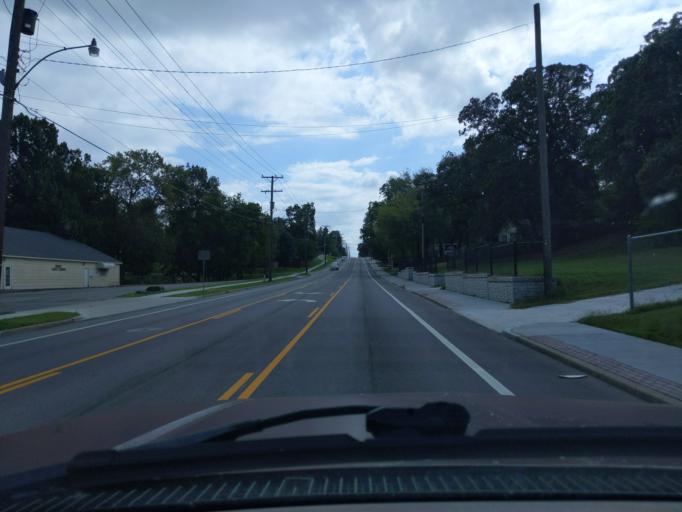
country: US
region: Oklahoma
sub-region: Tulsa County
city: Tulsa
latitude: 36.1009
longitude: -96.0116
